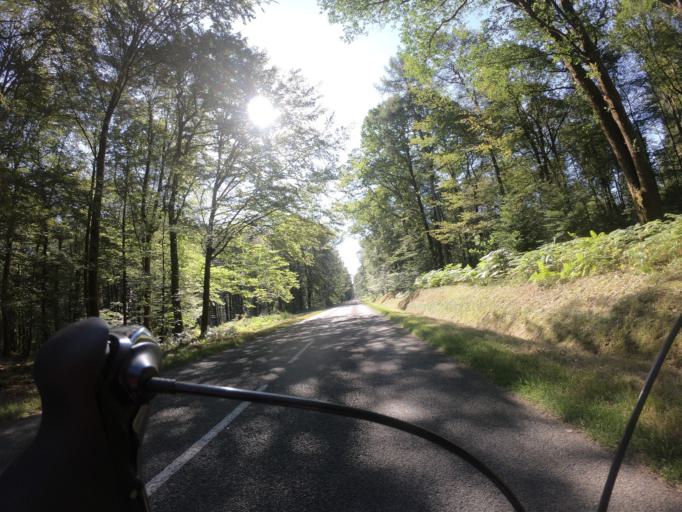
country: FR
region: Lower Normandy
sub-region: Departement de l'Orne
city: Juvigny-sous-Andaine
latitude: 48.5793
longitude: -0.4696
